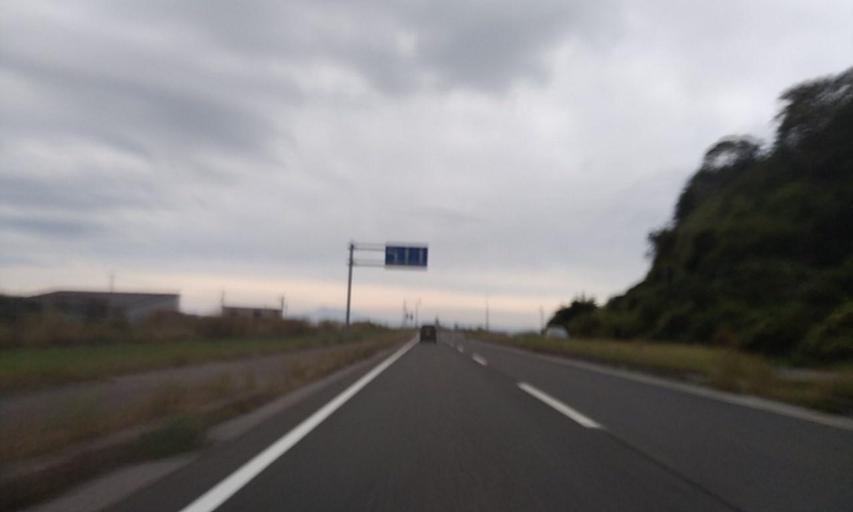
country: JP
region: Hokkaido
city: Abashiri
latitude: 44.0074
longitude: 144.2846
